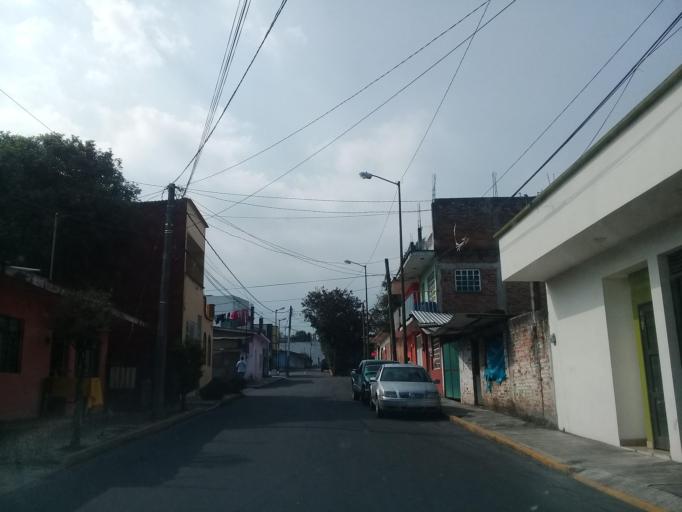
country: MX
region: Veracruz
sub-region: Ixhuatlancillo
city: Union y Progreso
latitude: 18.8674
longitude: -97.1037
